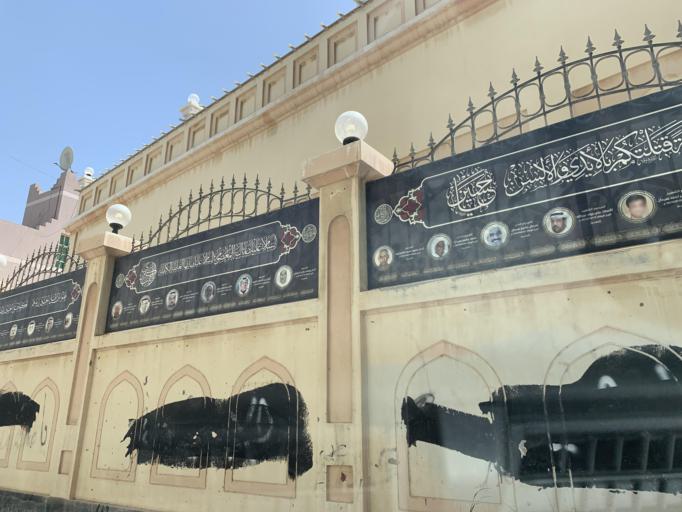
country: BH
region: Northern
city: Sitrah
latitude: 26.1433
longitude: 50.6100
